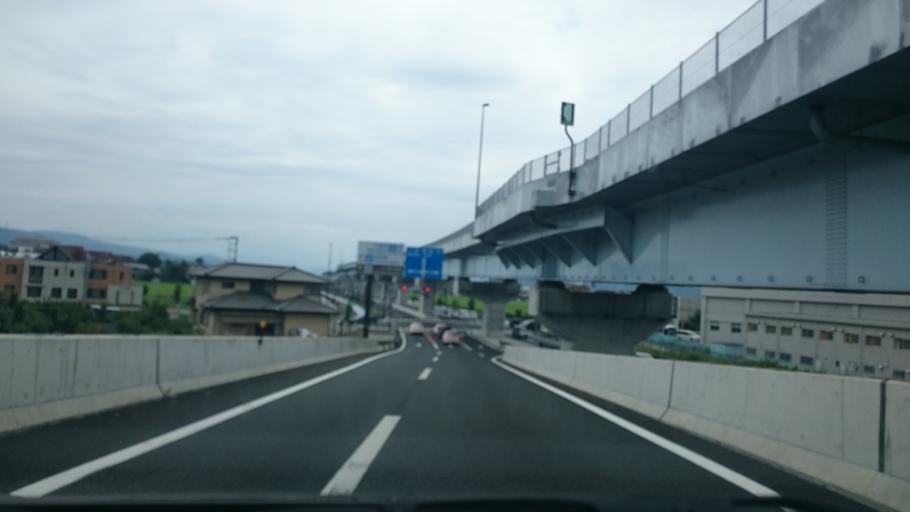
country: JP
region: Shizuoka
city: Mishima
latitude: 35.0960
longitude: 138.9464
